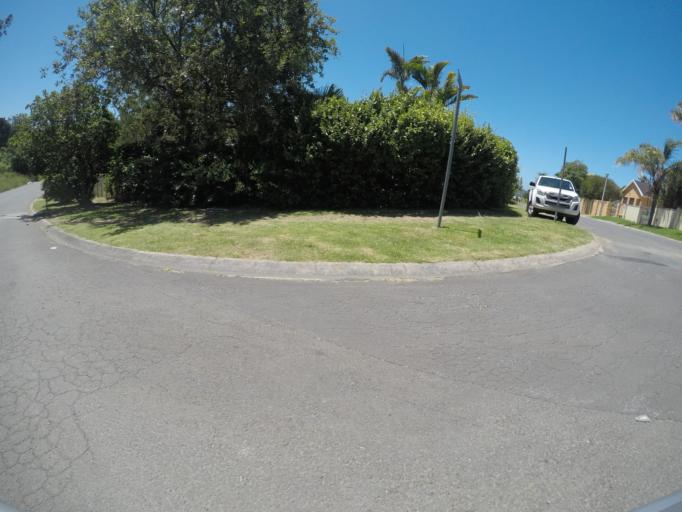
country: ZA
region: Eastern Cape
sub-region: Buffalo City Metropolitan Municipality
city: East London
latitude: -32.9563
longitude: 27.9372
